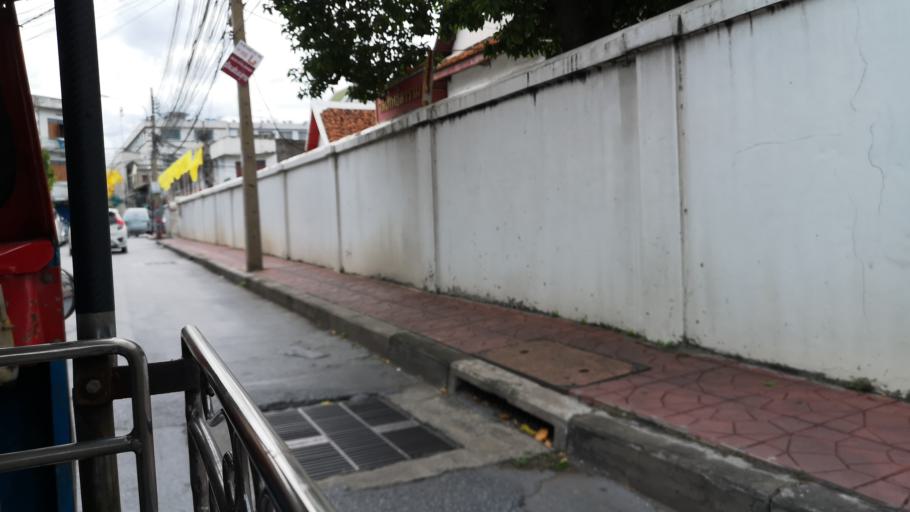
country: TH
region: Bangkok
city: Bangkok
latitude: 13.7529
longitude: 100.5035
